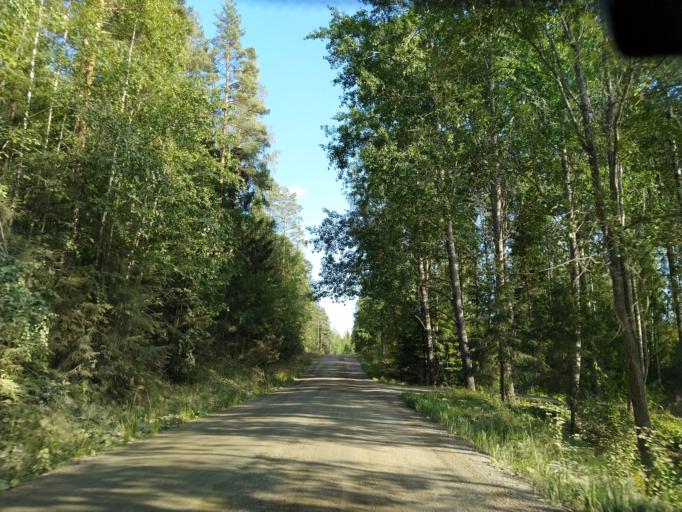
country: FI
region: Central Finland
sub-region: Jaemsae
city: Kuhmoinen
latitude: 61.7106
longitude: 24.9100
